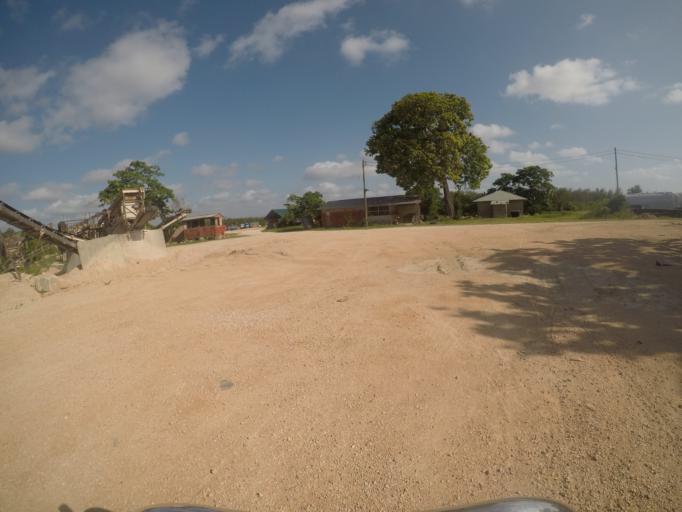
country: TZ
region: Zanzibar Central/South
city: Koani
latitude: -6.2161
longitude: 39.3335
